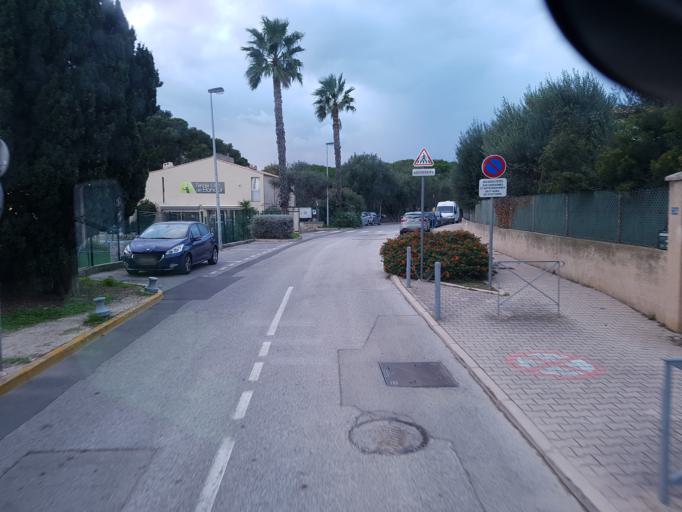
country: FR
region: Provence-Alpes-Cote d'Azur
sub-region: Departement du Var
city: Bandol
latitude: 43.1355
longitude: 5.7406
